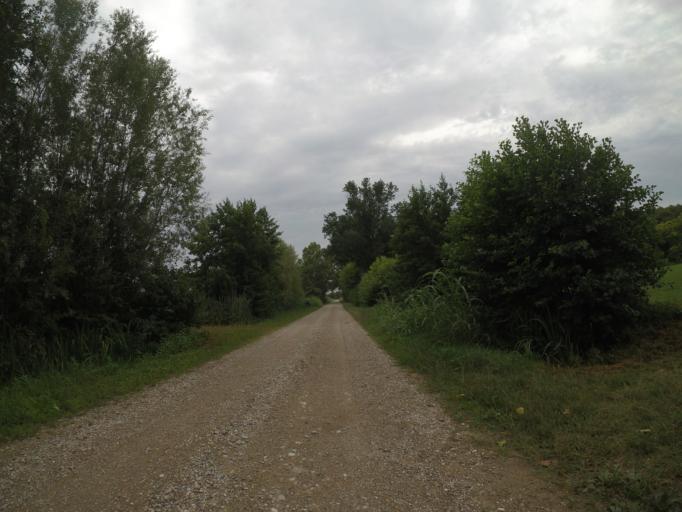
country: IT
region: Friuli Venezia Giulia
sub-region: Provincia di Udine
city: Bertiolo
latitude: 45.9088
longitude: 13.0614
